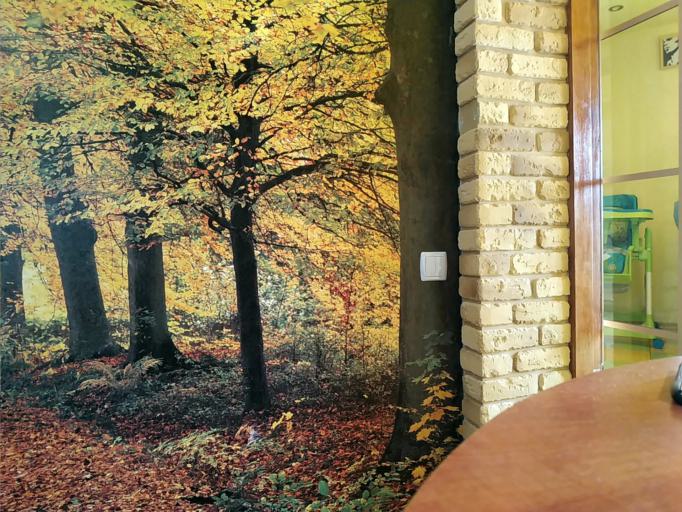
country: RU
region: Novgorod
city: Parfino
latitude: 57.7967
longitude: 31.6271
